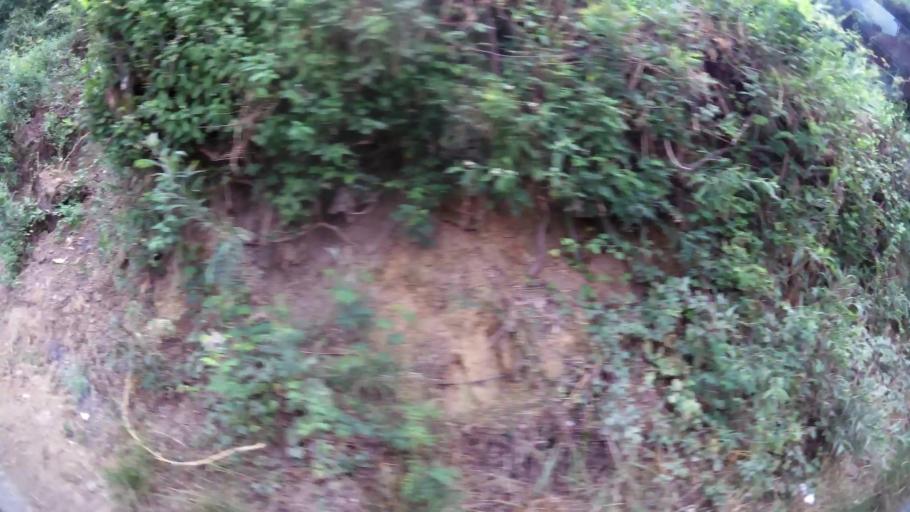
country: CL
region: Biobio
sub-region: Provincia de Concepcion
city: Concepcion
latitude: -36.8343
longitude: -73.0406
